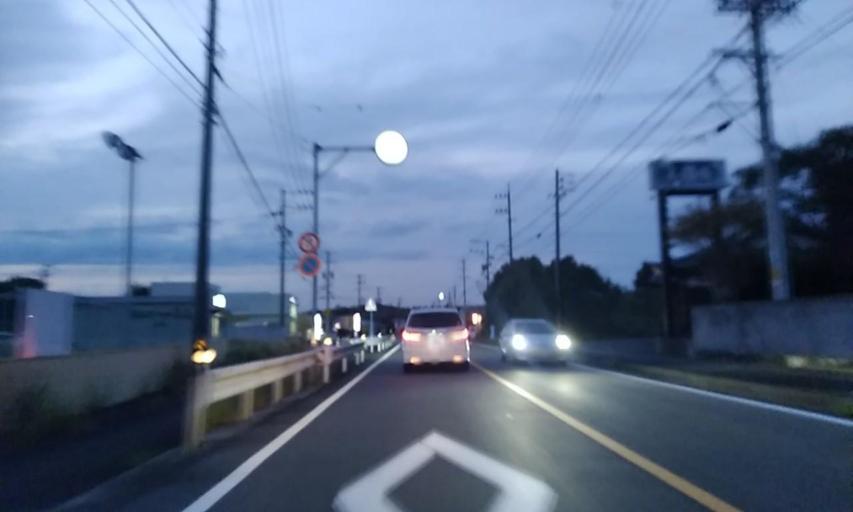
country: JP
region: Mie
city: Toba
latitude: 34.3059
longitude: 136.8732
